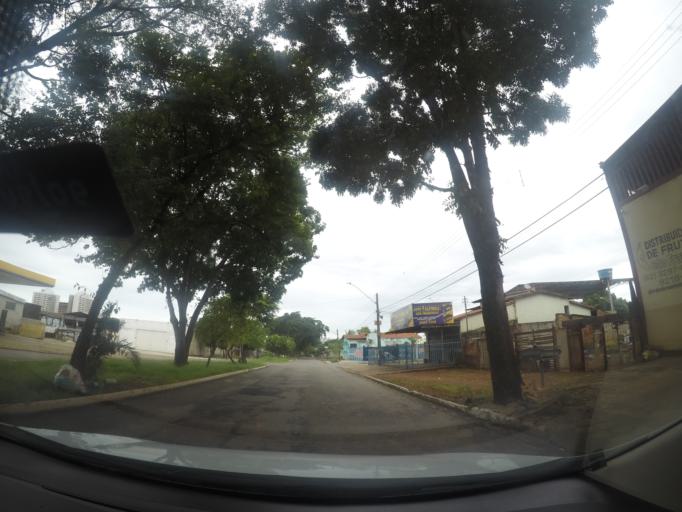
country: BR
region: Goias
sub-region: Goiania
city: Goiania
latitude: -16.6696
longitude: -49.3251
